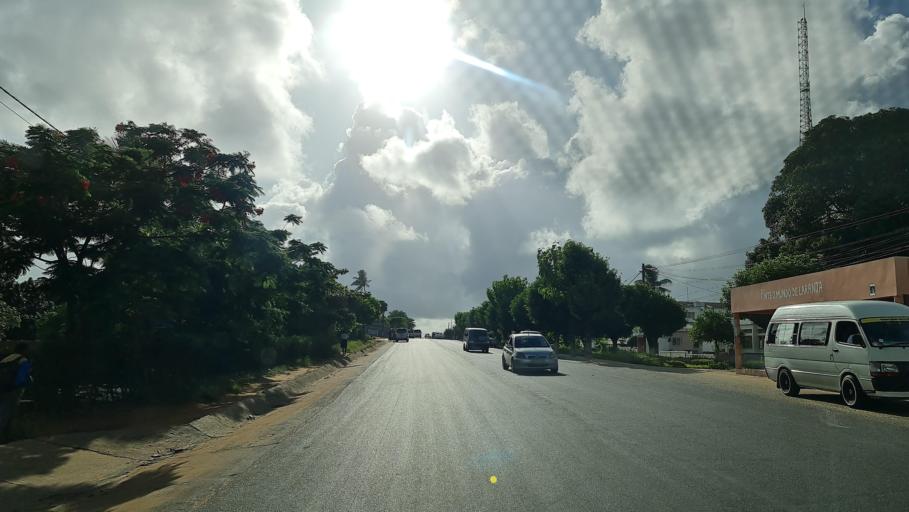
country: MZ
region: Gaza
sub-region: Xai-Xai District
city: Xai-Xai
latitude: -25.0568
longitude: 33.6540
